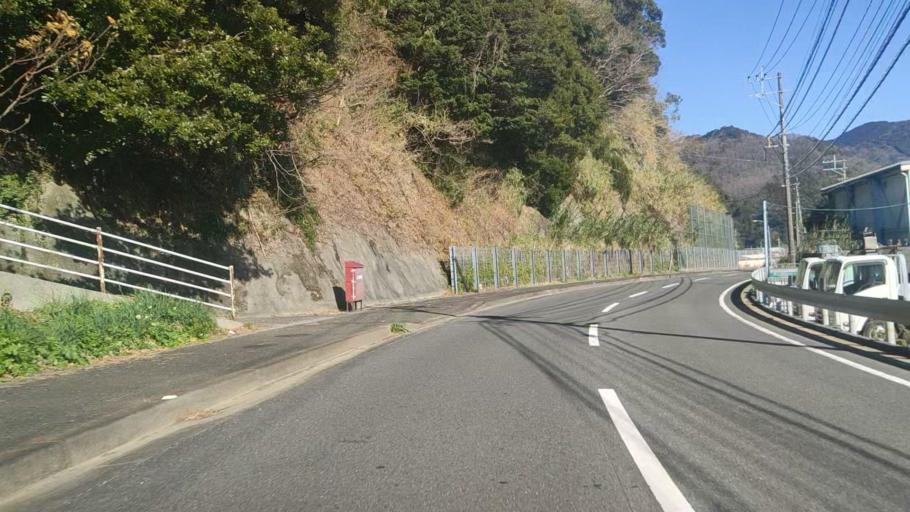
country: JP
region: Oita
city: Saiki
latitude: 32.7989
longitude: 131.9188
